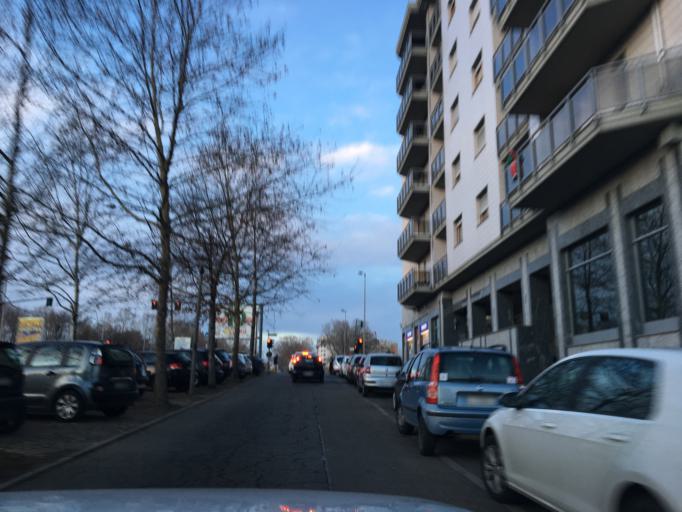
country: IT
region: Piedmont
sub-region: Provincia di Torino
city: Lesna
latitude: 45.0546
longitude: 7.6350
